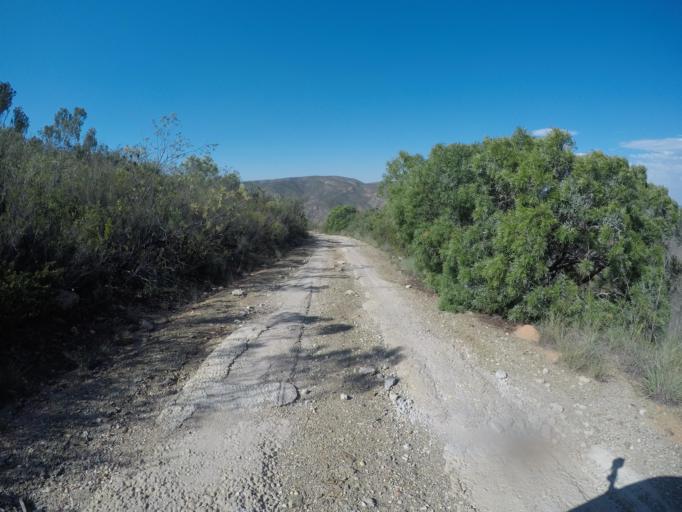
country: ZA
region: Eastern Cape
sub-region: Cacadu District Municipality
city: Kareedouw
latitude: -33.6392
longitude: 24.4522
